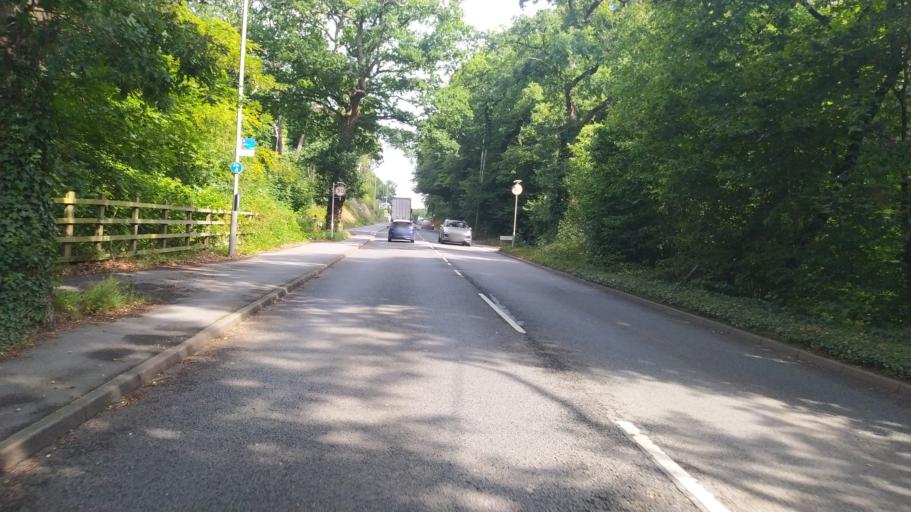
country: GB
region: England
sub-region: Dorset
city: Wimborne Minster
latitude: 50.7753
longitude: -1.9781
